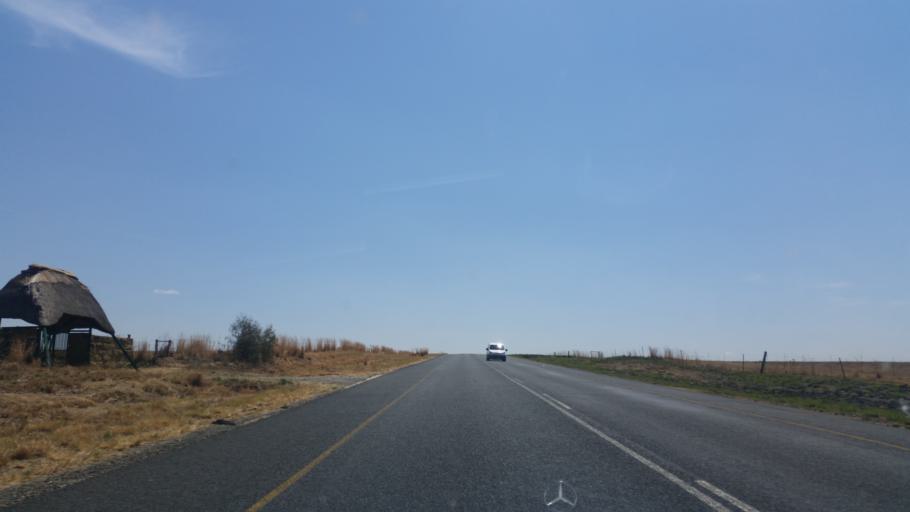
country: ZA
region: Orange Free State
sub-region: Thabo Mofutsanyana District Municipality
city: Phuthaditjhaba
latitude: -28.1900
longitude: 28.6864
